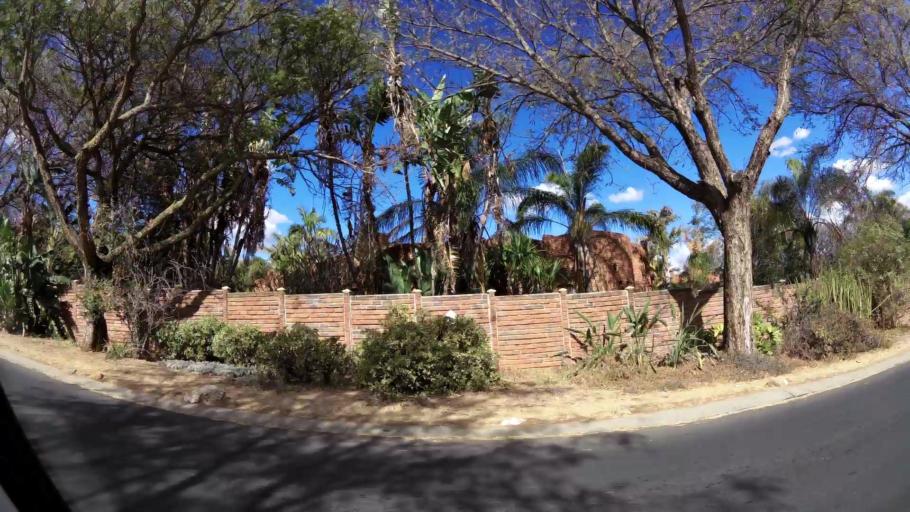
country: ZA
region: Limpopo
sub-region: Capricorn District Municipality
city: Polokwane
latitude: -23.8888
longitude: 29.4791
